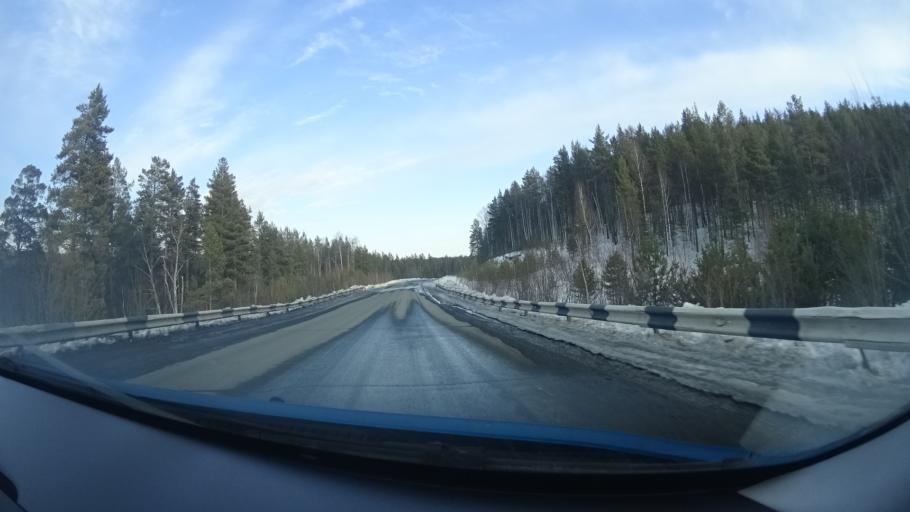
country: RU
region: Bashkortostan
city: Lomovka
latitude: 53.5241
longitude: 58.2842
